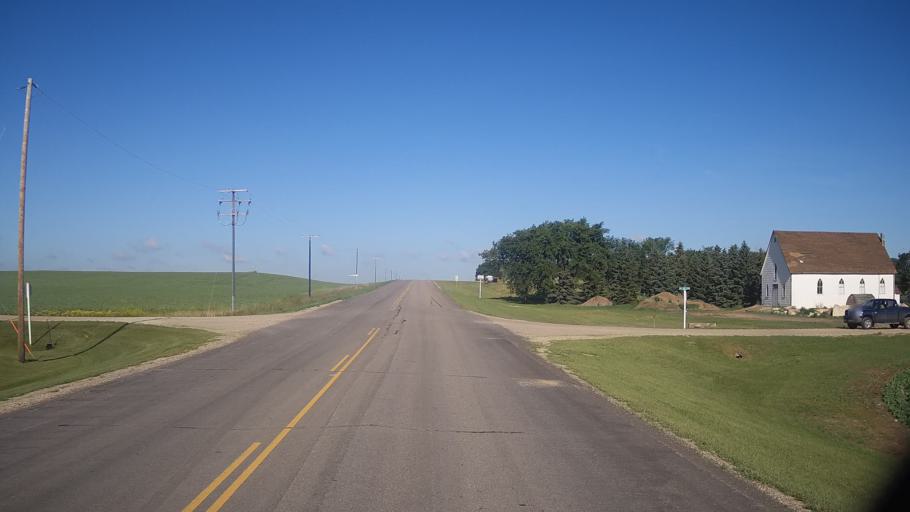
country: CA
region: Saskatchewan
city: Watrous
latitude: 51.6781
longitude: -105.4038
